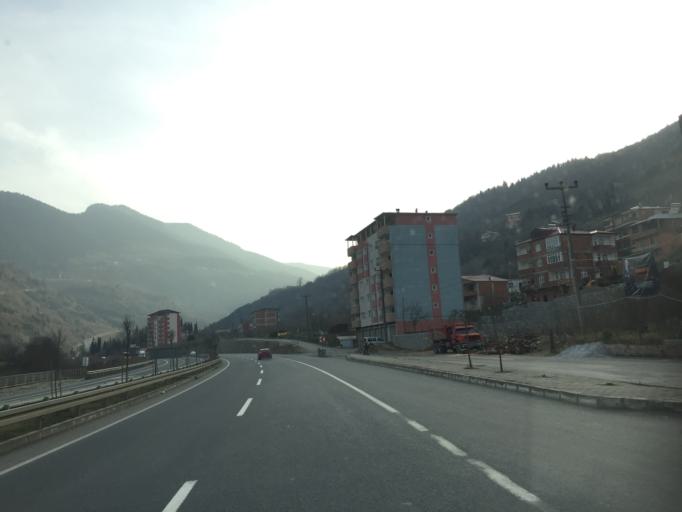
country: TR
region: Trabzon
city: Esiroglu
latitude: 40.8735
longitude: 39.6845
